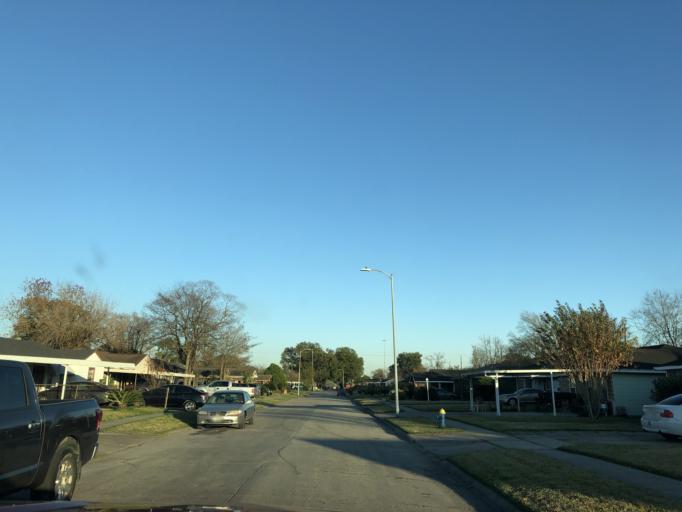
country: US
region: Texas
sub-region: Harris County
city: Jacinto City
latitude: 29.7610
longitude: -95.2715
